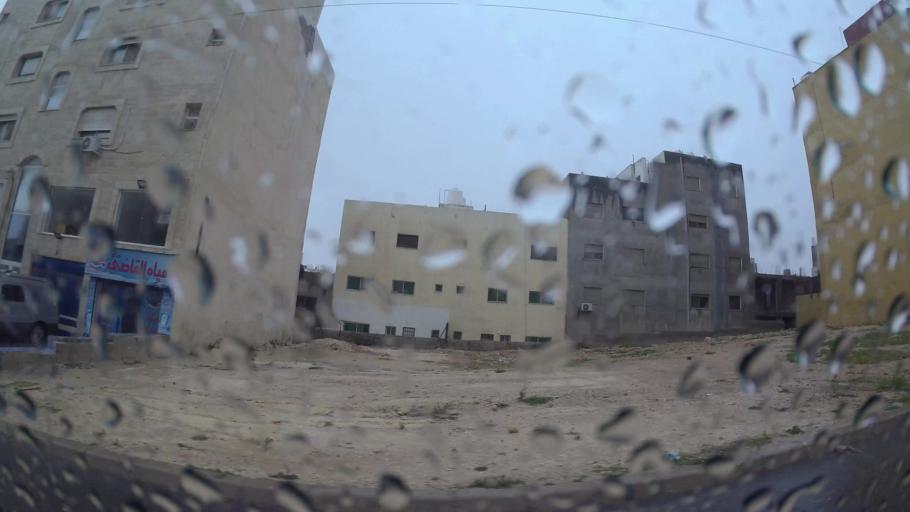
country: JO
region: Amman
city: Al Jubayhah
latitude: 32.0495
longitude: 35.8825
